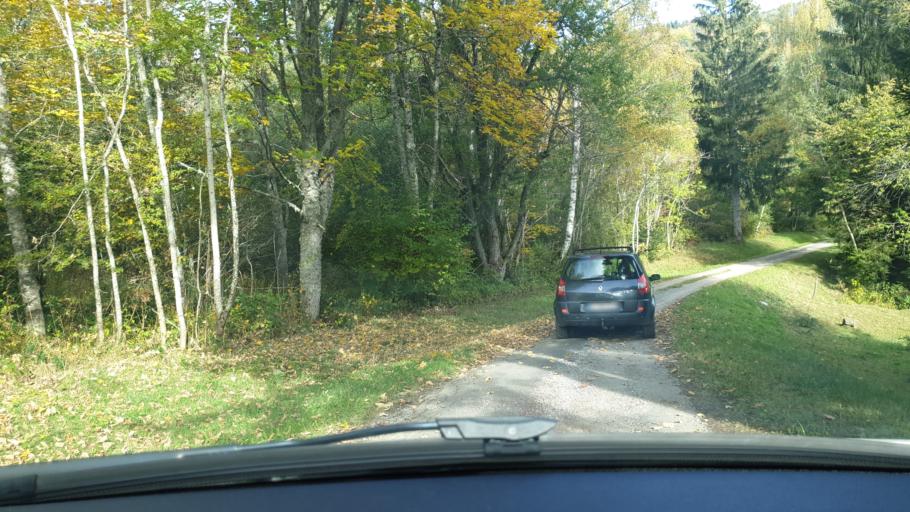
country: FR
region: Rhone-Alpes
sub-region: Departement de la Savoie
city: Aiton
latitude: 45.4991
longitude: 6.2222
